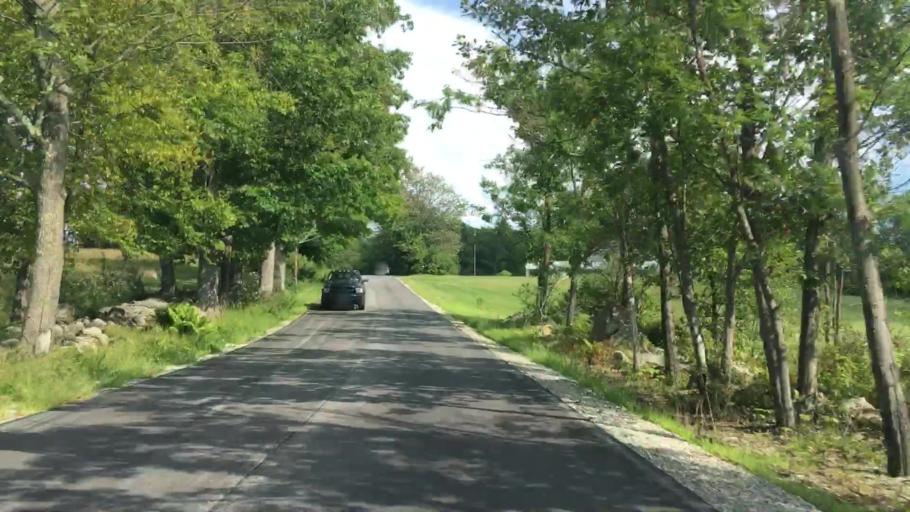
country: US
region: New Hampshire
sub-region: Belknap County
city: Sanbornton
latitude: 43.5057
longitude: -71.6078
